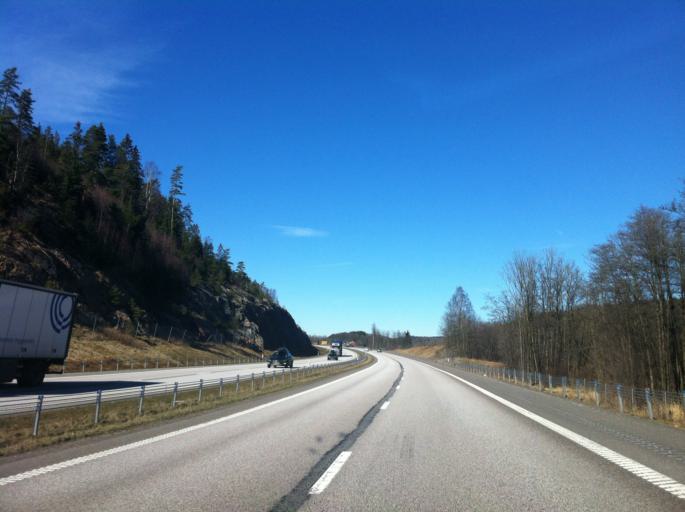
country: SE
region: Vaestra Goetaland
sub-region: Munkedals Kommun
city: Munkedal
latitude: 58.3736
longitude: 11.7854
